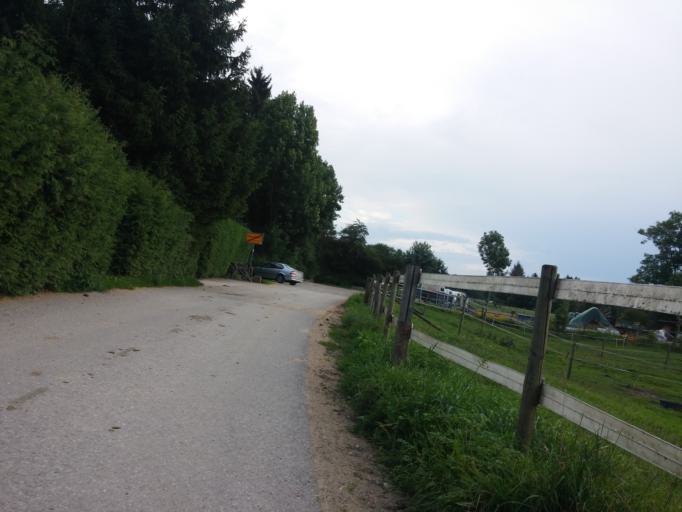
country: DE
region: Bavaria
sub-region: Swabia
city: Buxheim
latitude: 47.9913
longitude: 10.1229
